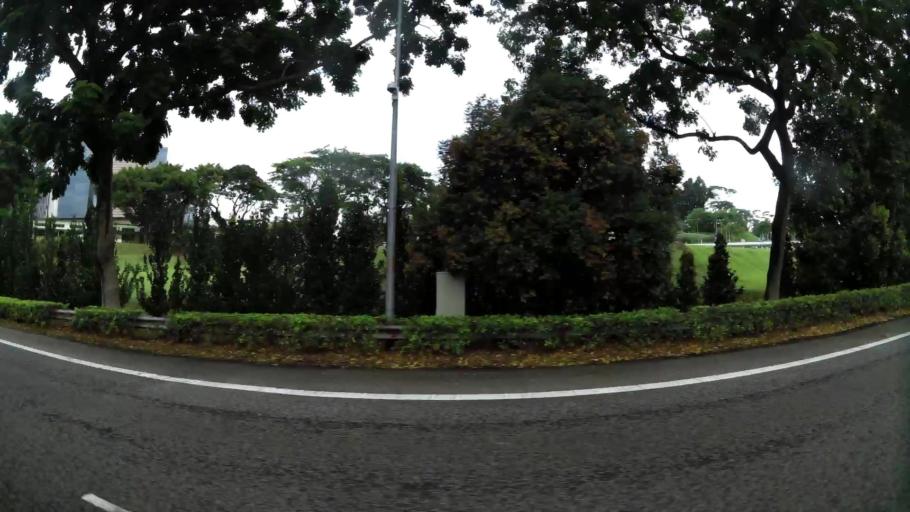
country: SG
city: Singapore
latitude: 1.2817
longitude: 103.8322
